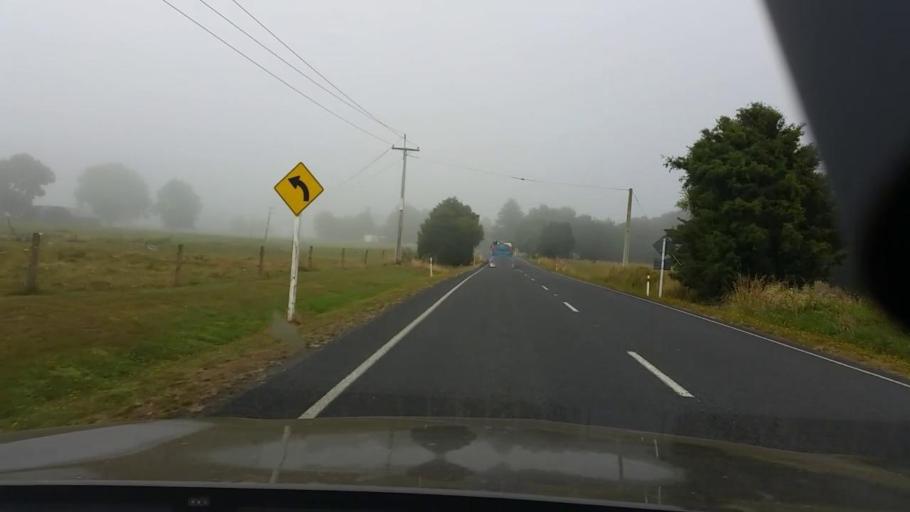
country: NZ
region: Waikato
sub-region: Waikato District
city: Ngaruawahia
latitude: -37.6387
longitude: 175.2963
